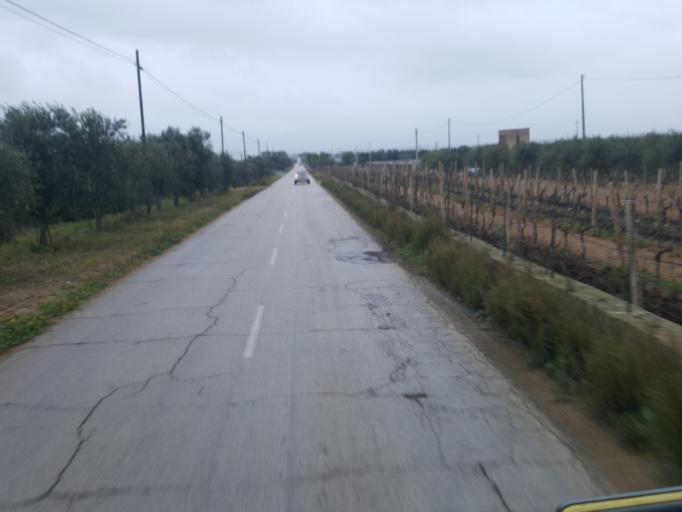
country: IT
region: Apulia
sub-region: Provincia di Taranto
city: Montemesola
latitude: 40.5456
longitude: 17.3671
